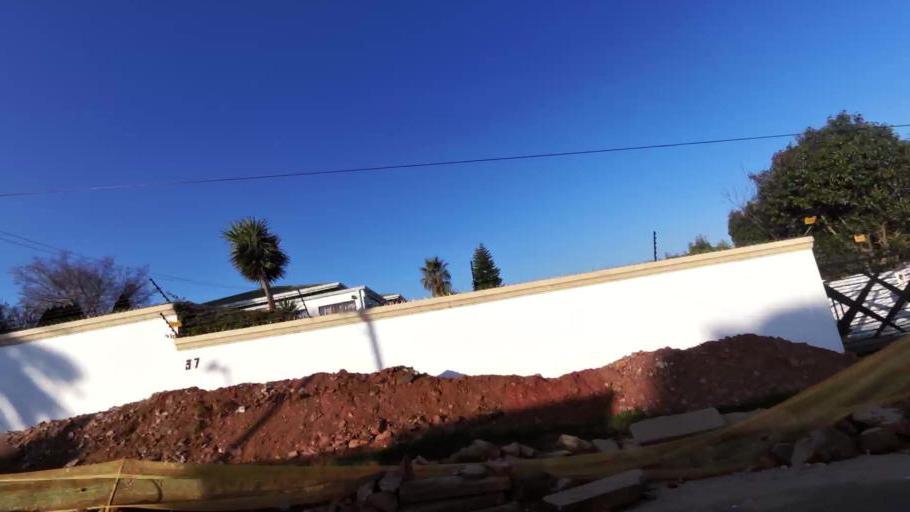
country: ZA
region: Gauteng
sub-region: City of Johannesburg Metropolitan Municipality
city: Roodepoort
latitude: -26.1719
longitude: 27.9454
